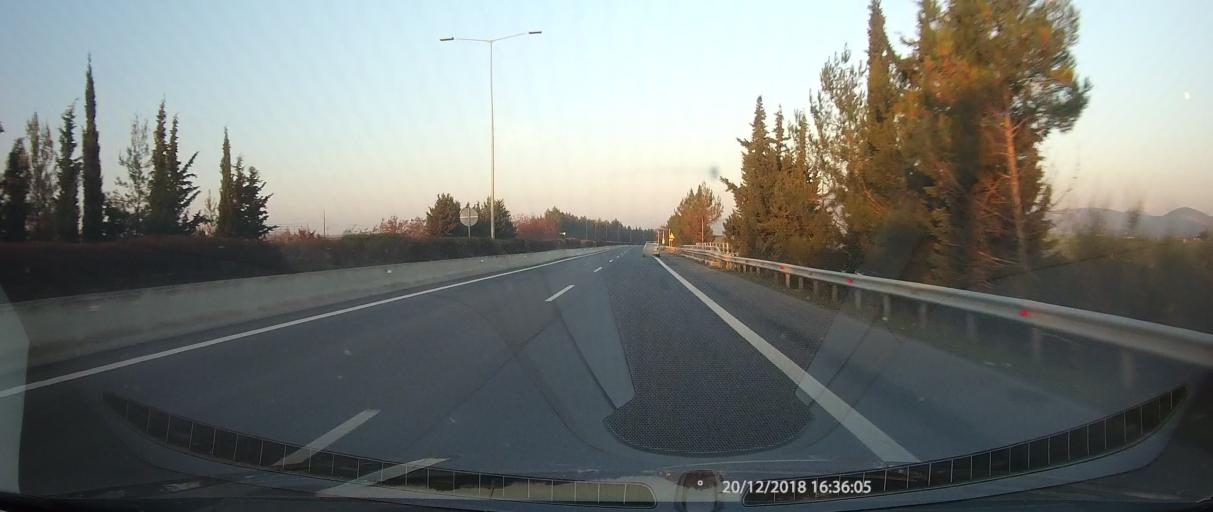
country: GR
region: Thessaly
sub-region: Nomos Magnisias
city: Velestino
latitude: 39.3139
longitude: 22.7509
